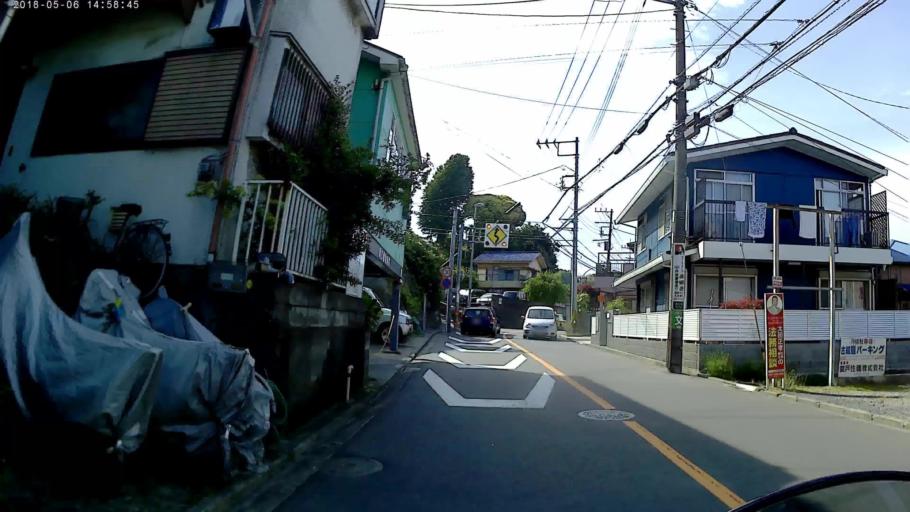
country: JP
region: Kanagawa
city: Yokohama
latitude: 35.4179
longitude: 139.6167
